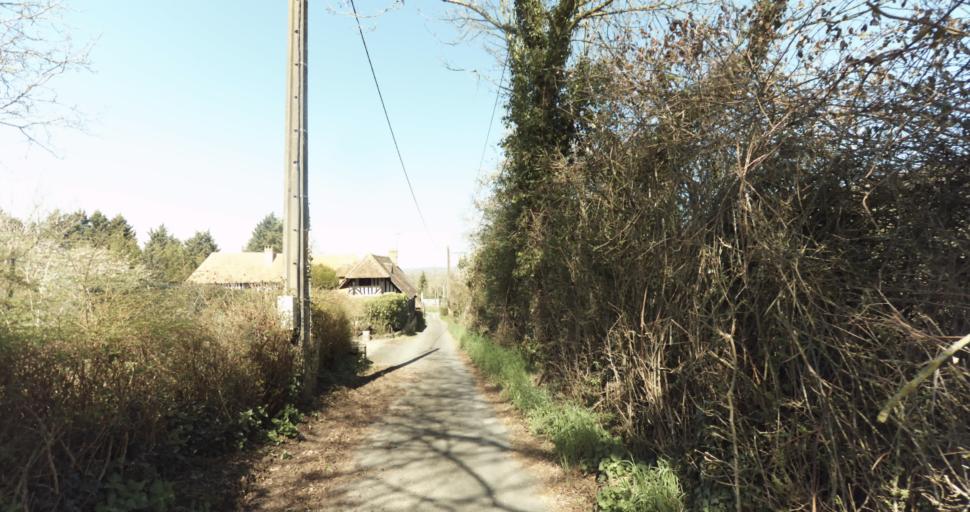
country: FR
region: Lower Normandy
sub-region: Departement du Calvados
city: Saint-Pierre-sur-Dives
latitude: 49.0043
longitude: 0.0356
